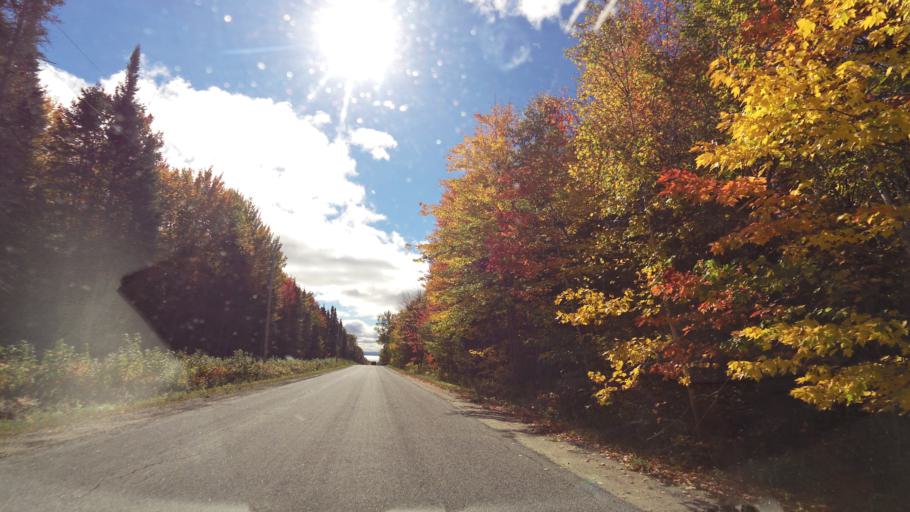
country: CA
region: Ontario
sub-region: Nipissing District
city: North Bay
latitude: 46.3523
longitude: -79.4872
